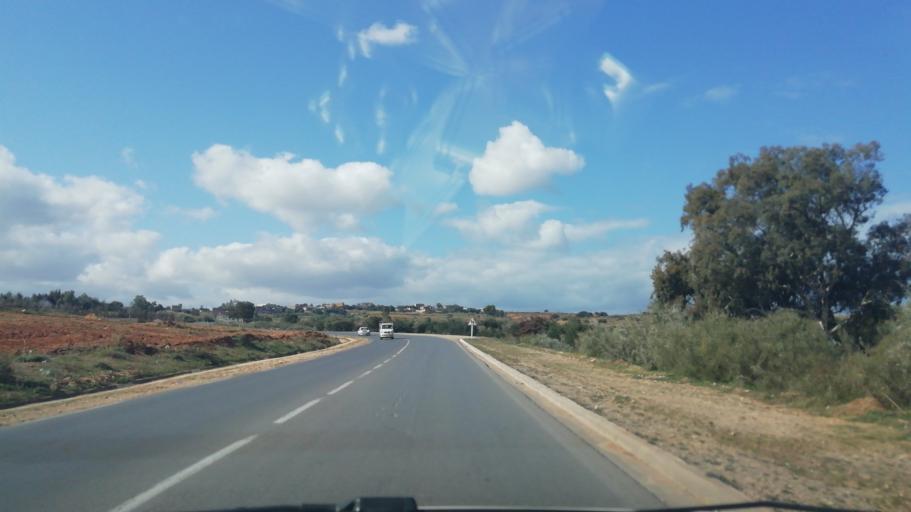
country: DZ
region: Relizane
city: Mazouna
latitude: 36.2918
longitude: 0.6538
